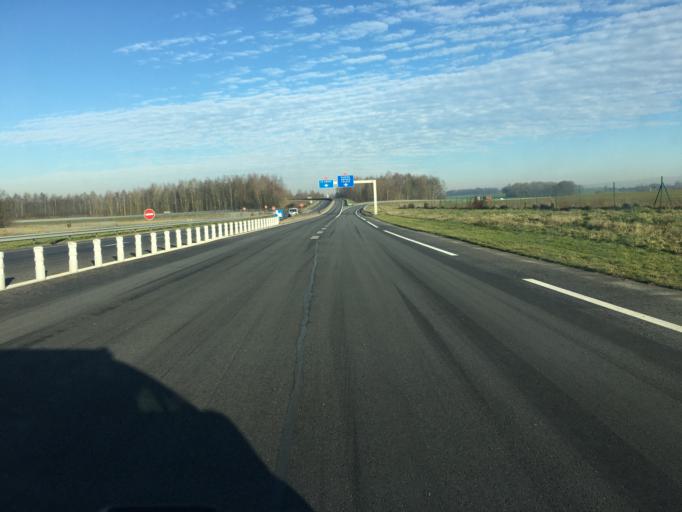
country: FR
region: Haute-Normandie
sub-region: Departement de la Seine-Maritime
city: Yerville
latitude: 49.6486
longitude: 0.8435
